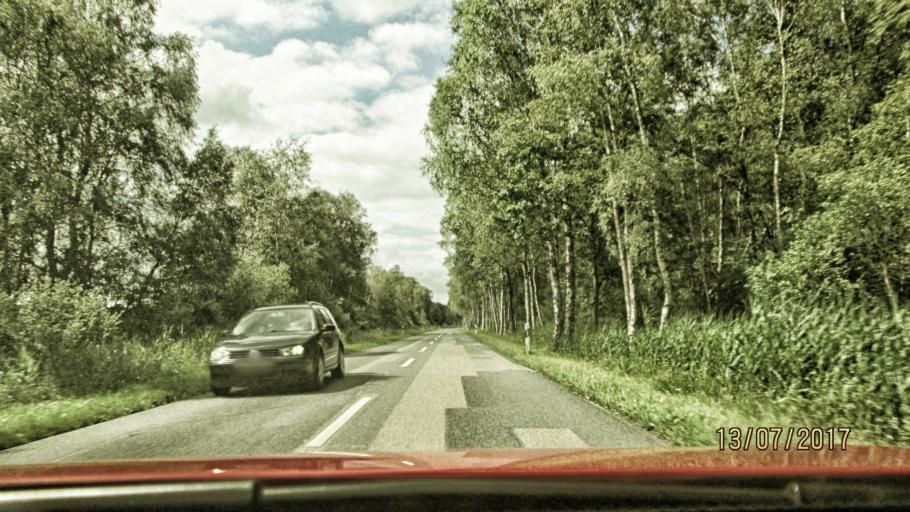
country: DE
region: Lower Saxony
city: Sassenburg
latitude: 52.5664
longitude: 10.6236
